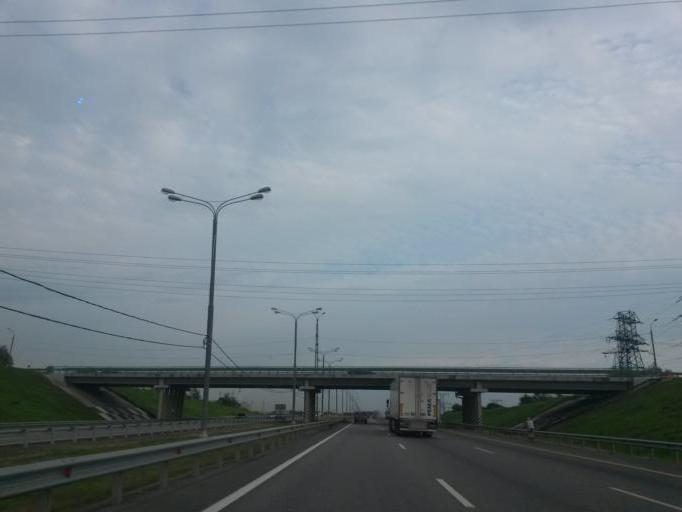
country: RU
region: Moskovskaya
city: Vostryakovo
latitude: 55.3789
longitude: 37.7784
